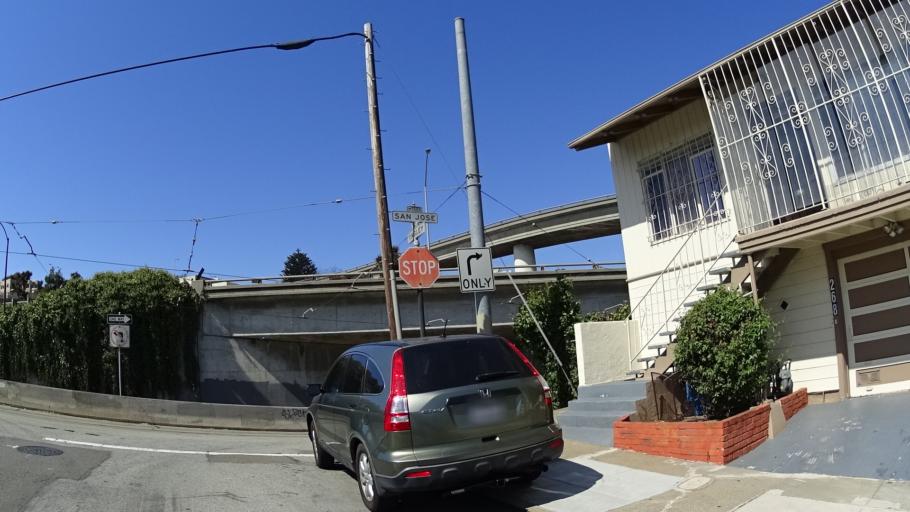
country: US
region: California
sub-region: San Mateo County
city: Daly City
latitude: 37.7306
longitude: -122.4355
